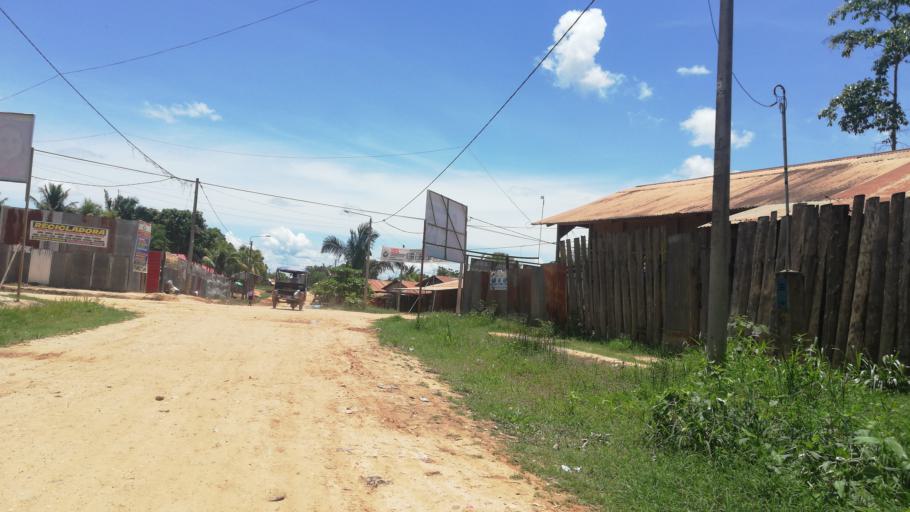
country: PE
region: Ucayali
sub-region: Provincia de Coronel Portillo
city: Puerto Callao
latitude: -8.3591
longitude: -74.5915
